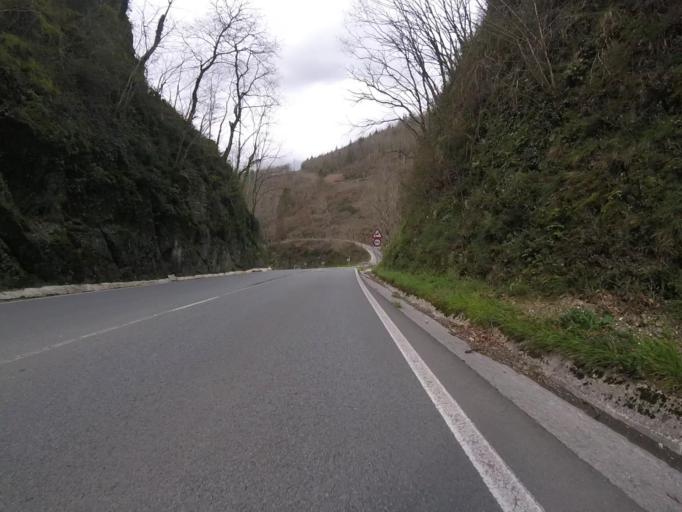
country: ES
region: Navarre
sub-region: Provincia de Navarra
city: Etxalar
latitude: 43.2370
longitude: -1.6544
